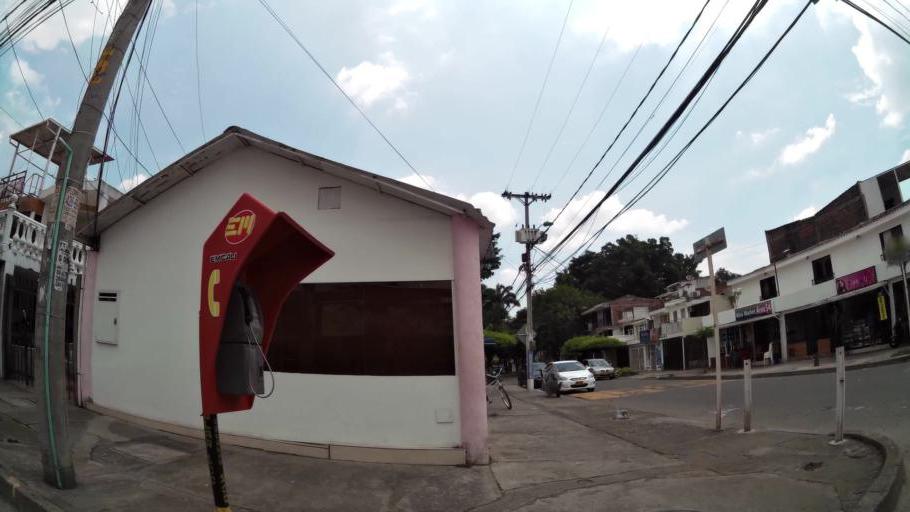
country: CO
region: Valle del Cauca
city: Cali
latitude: 3.4743
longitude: -76.5014
